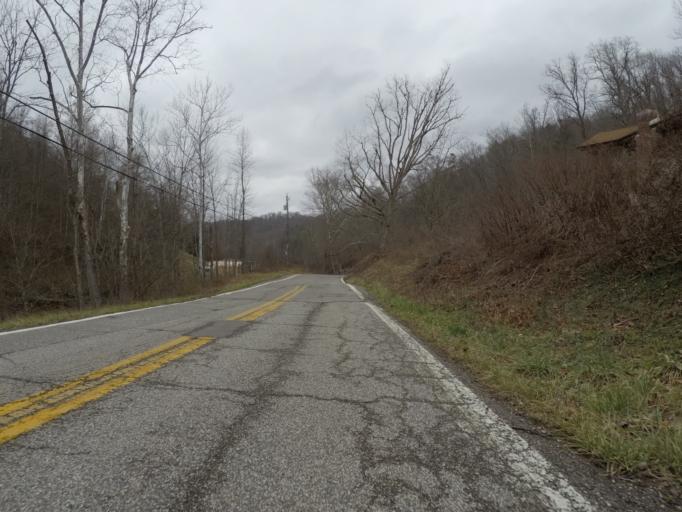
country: US
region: West Virginia
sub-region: Cabell County
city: Lesage
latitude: 38.4650
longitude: -82.2782
